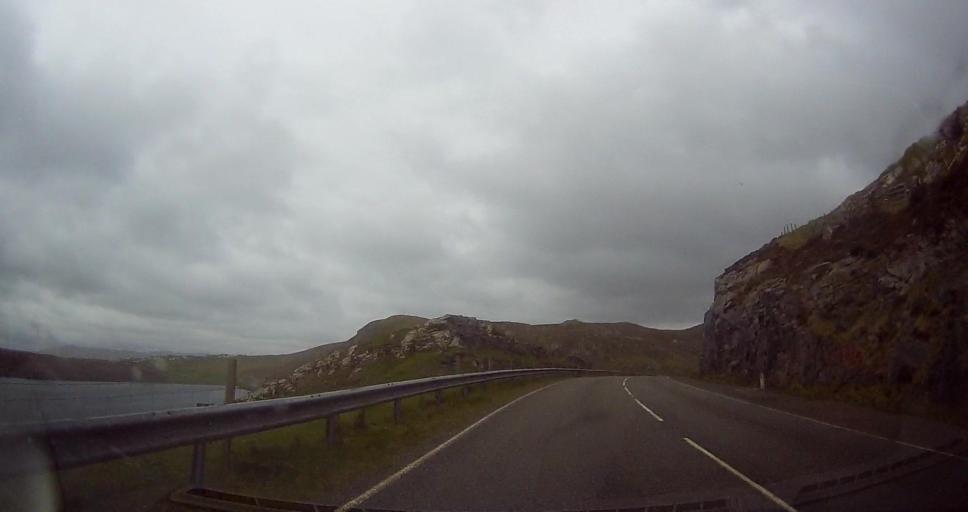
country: GB
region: Scotland
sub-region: Shetland Islands
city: Lerwick
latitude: 60.4013
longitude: -1.3835
